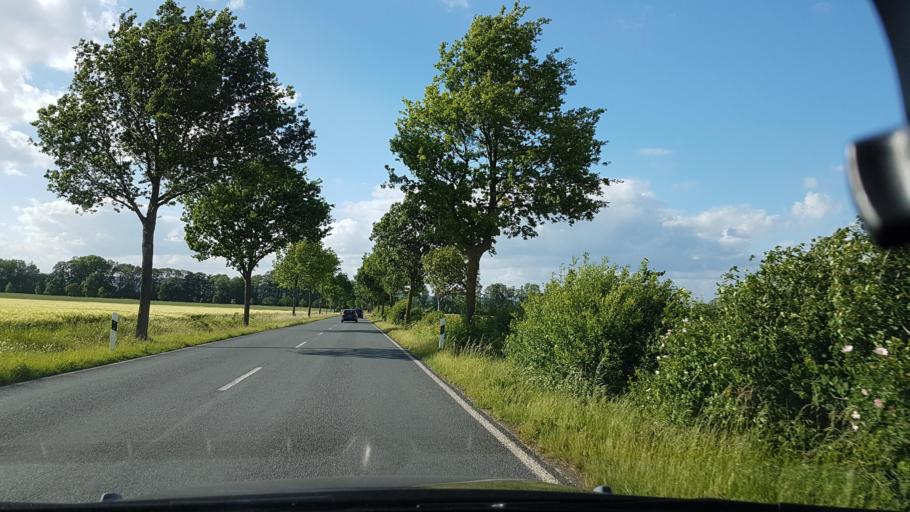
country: DE
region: Lower Saxony
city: Elze
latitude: 52.1507
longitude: 9.6660
